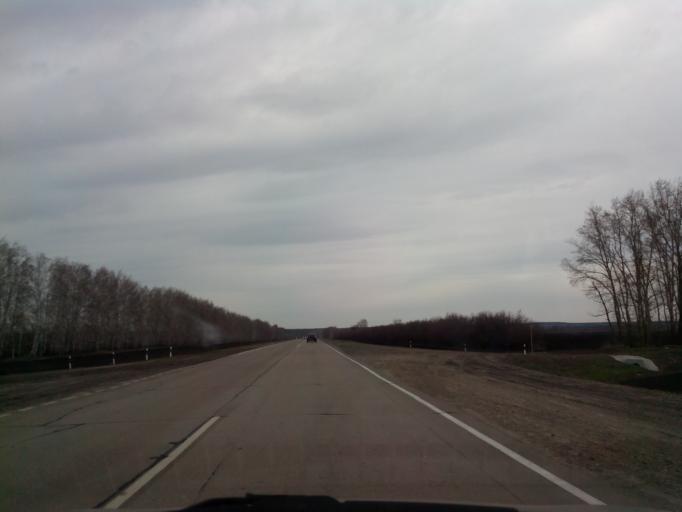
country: RU
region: Tambov
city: Znamenka
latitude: 52.5053
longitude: 41.3641
